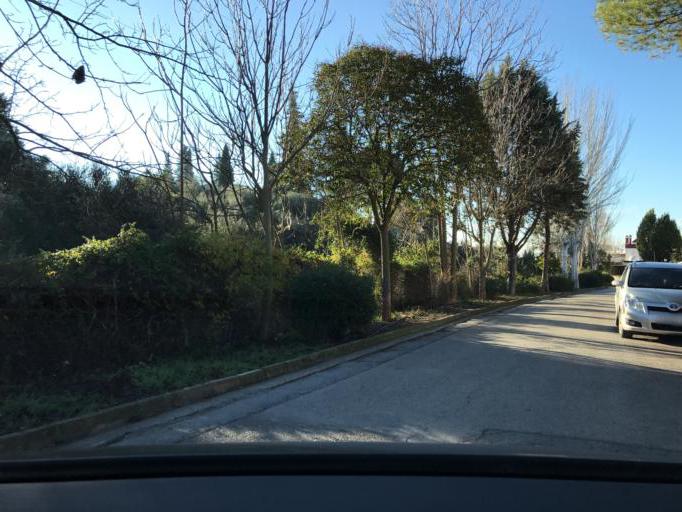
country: ES
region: Andalusia
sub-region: Provincia de Granada
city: Albolote
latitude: 37.2524
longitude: -3.6551
